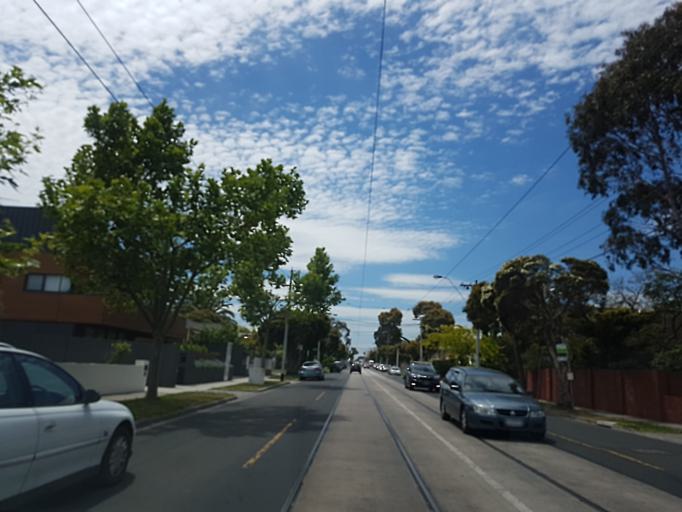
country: AU
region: Victoria
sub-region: Glen Eira
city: Caulfield
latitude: -37.8831
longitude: 145.0227
